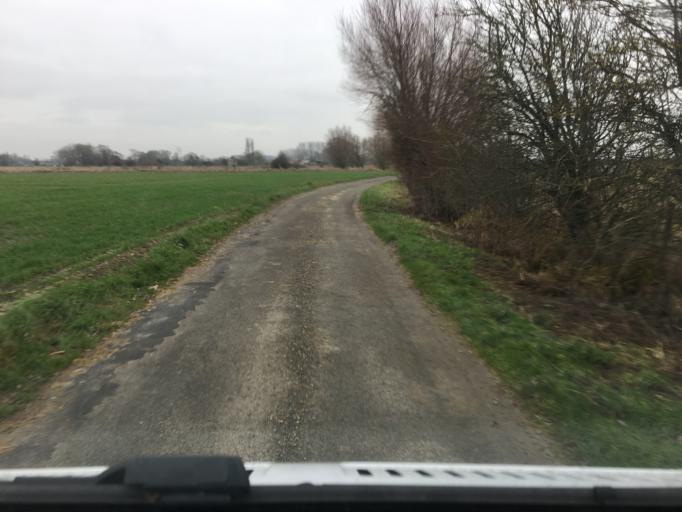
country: FR
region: Picardie
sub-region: Departement de la Somme
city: Pende
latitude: 50.1783
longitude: 1.5432
